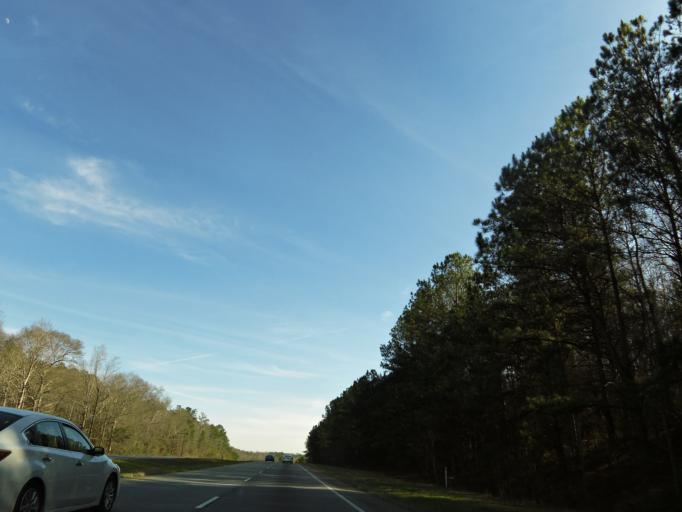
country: US
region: Georgia
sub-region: Chattahoochee County
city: Cusseta
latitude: 32.2570
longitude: -84.7253
